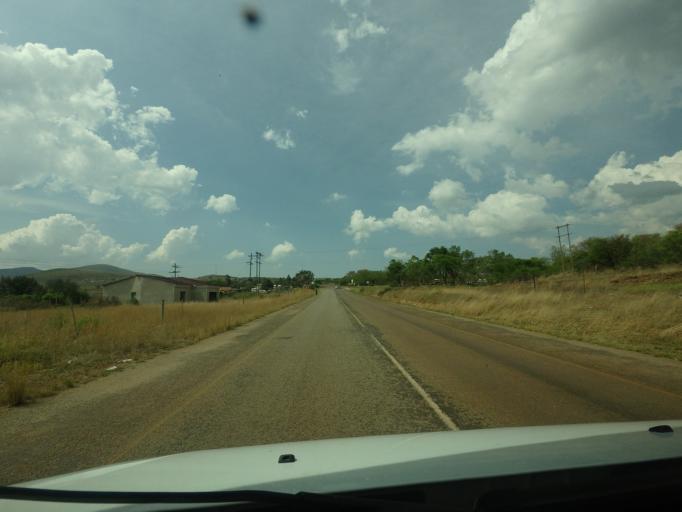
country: ZA
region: Mpumalanga
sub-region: Ehlanzeni District
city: Graksop
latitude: -24.6738
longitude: 30.8058
